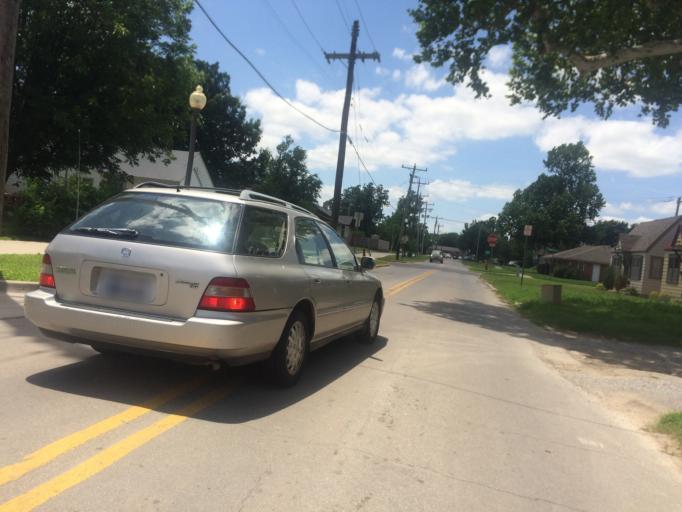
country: US
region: Oklahoma
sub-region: Cleveland County
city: Norman
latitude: 35.2143
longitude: -97.4406
